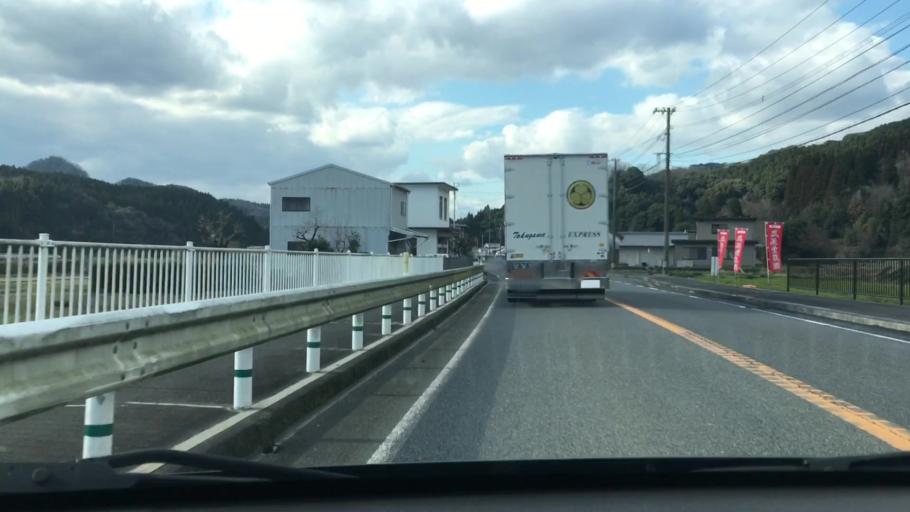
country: JP
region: Oita
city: Usuki
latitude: 33.0057
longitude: 131.7242
